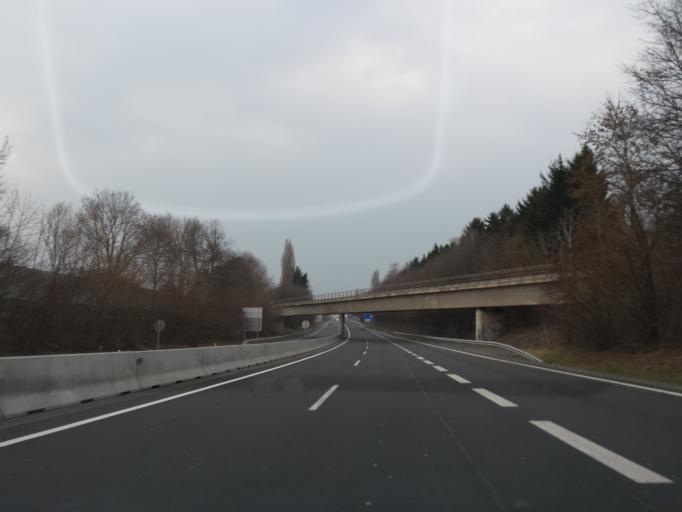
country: AT
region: Styria
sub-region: Politischer Bezirk Graz-Umgebung
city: Raaba
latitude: 47.0356
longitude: 15.4754
